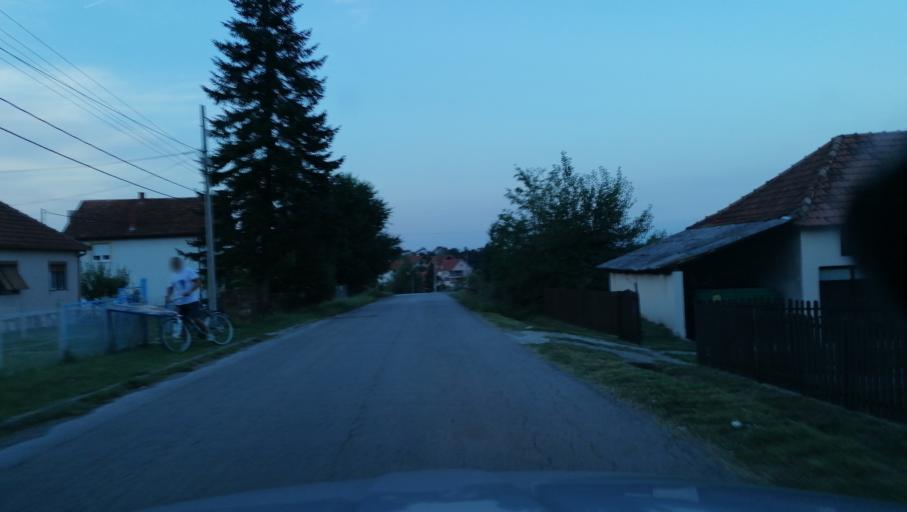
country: RS
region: Central Serbia
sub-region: Kolubarski Okrug
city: Valjevo
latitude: 44.2544
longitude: 19.8758
